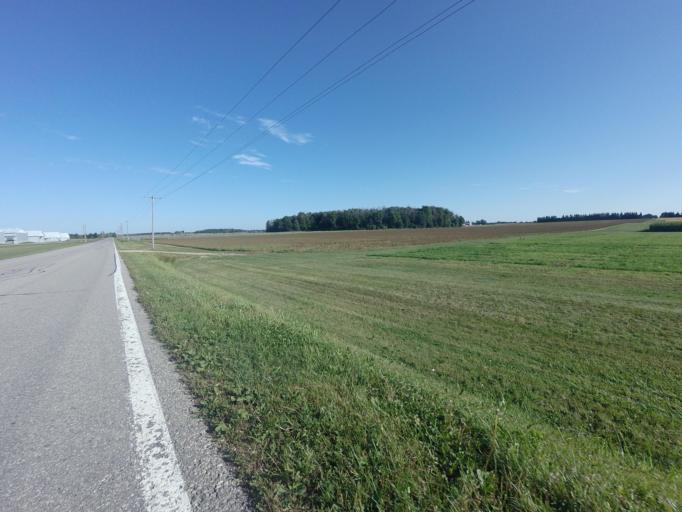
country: CA
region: Ontario
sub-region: Wellington County
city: Guelph
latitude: 43.6440
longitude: -80.4067
